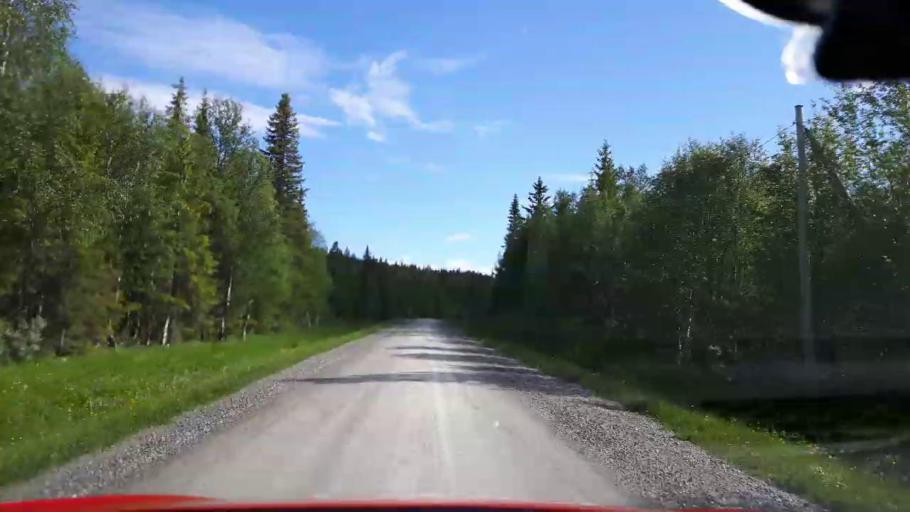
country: SE
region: Jaemtland
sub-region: Krokoms Kommun
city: Valla
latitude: 63.7870
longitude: 14.0480
